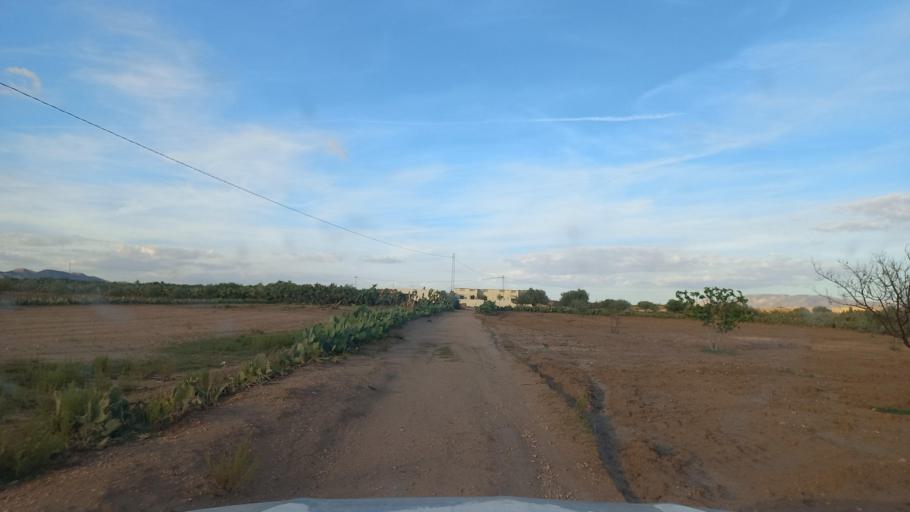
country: TN
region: Al Qasrayn
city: Sbiba
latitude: 35.3530
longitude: 9.0326
